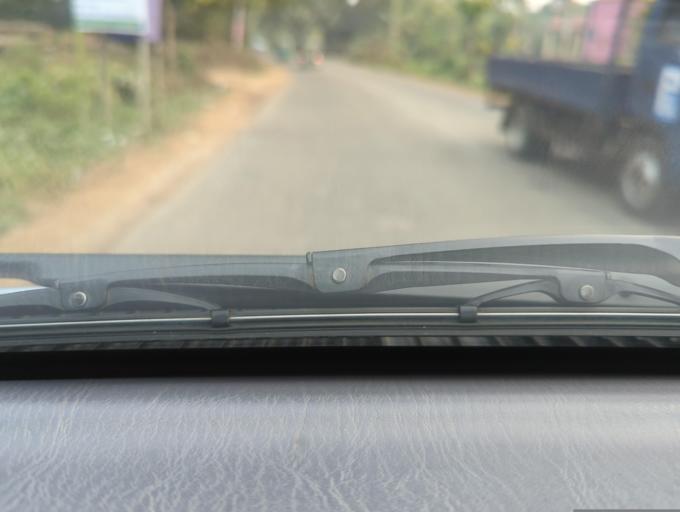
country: BD
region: Sylhet
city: Maulavi Bazar
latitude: 24.4981
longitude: 91.7363
